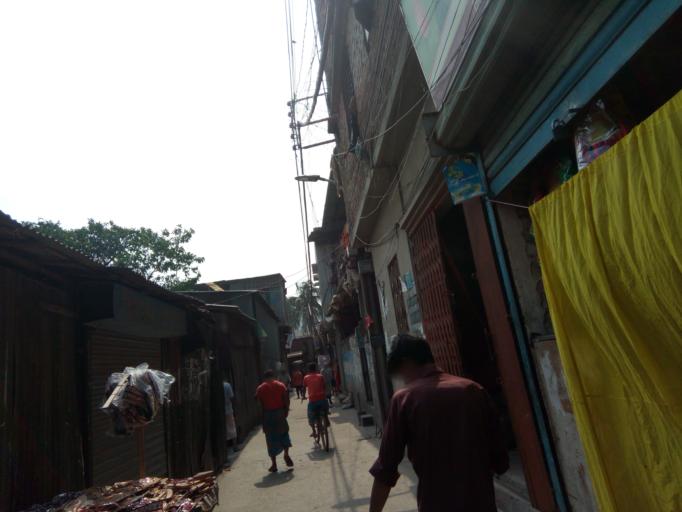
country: BD
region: Dhaka
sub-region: Dhaka
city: Dhaka
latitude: 23.6934
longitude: 90.4294
